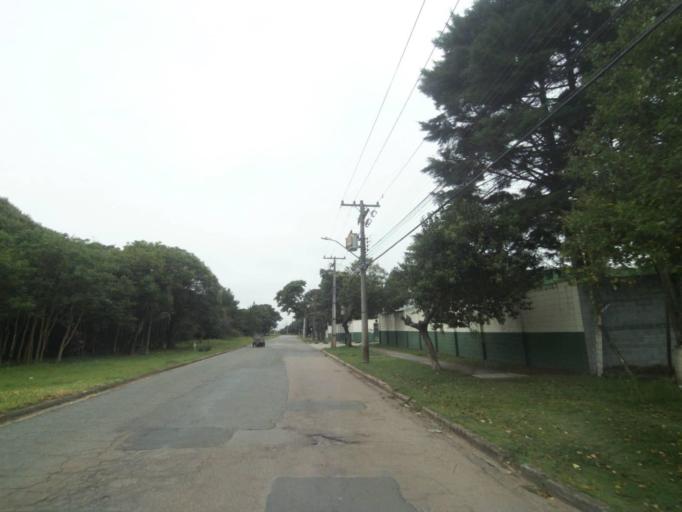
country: BR
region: Parana
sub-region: Araucaria
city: Araucaria
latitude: -25.5410
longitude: -49.3236
